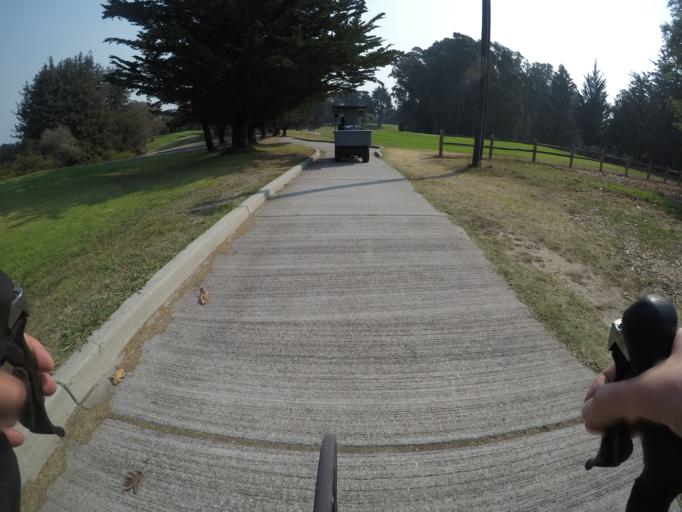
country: US
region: California
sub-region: Santa Cruz County
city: Live Oak
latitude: 36.9960
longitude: -121.9964
